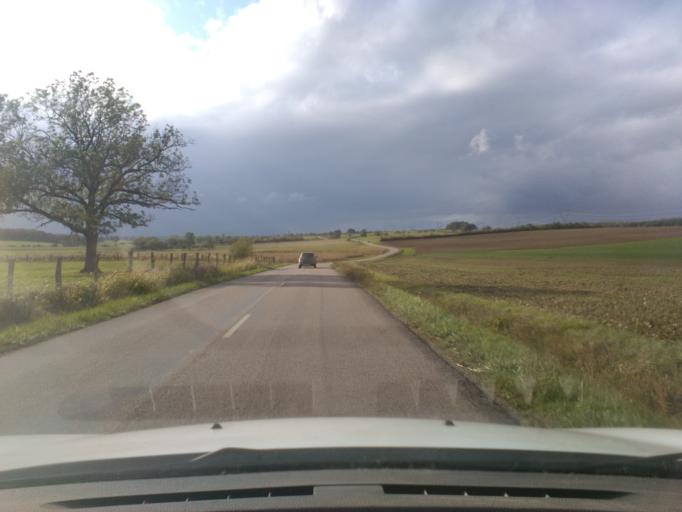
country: FR
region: Lorraine
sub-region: Departement des Vosges
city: Aydoilles
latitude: 48.2506
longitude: 6.5939
